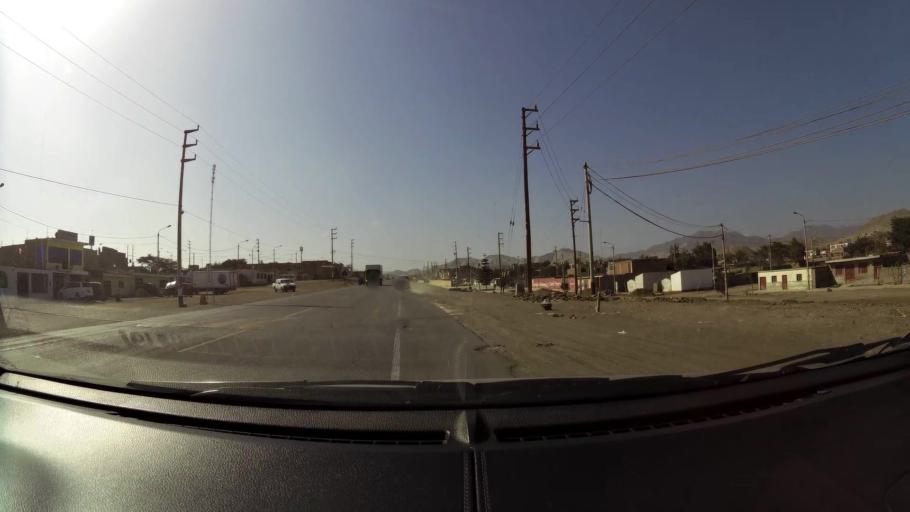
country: PE
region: Ancash
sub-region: Provincia de Huarmey
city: Huarmey
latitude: -10.0553
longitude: -78.1580
